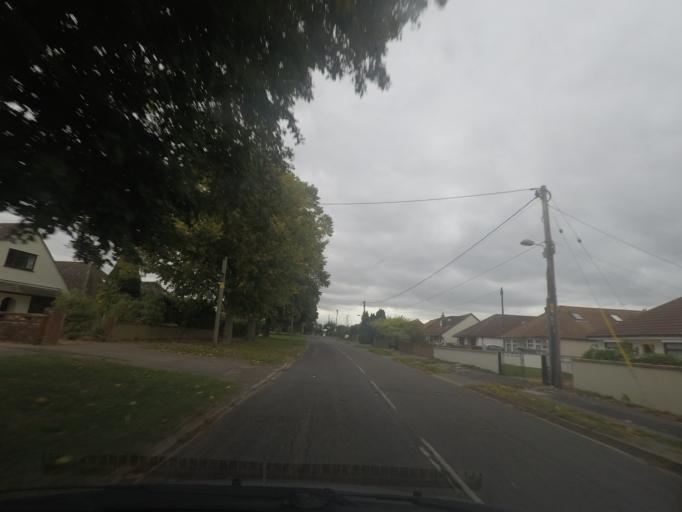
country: GB
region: England
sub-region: Oxfordshire
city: Sutton Courtenay
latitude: 51.6329
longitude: -1.2824
